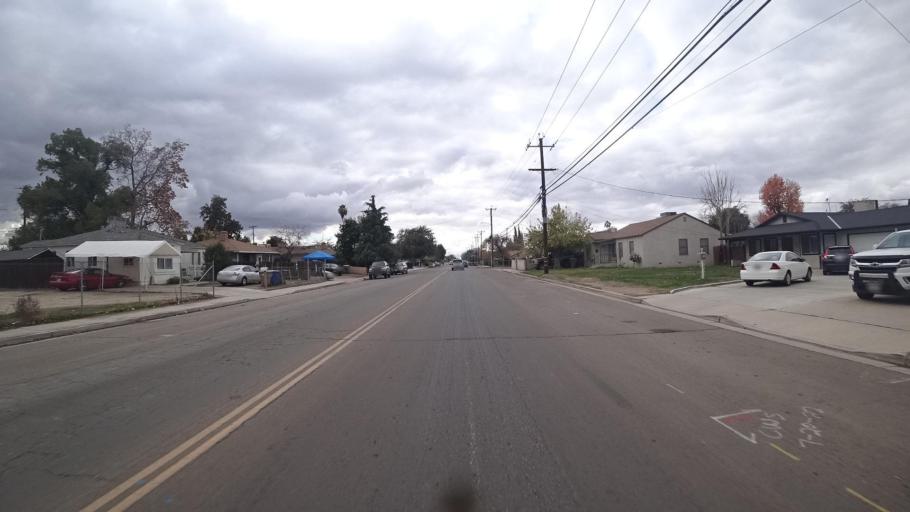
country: US
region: California
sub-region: Kern County
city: Bakersfield
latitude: 35.3467
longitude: -119.0237
